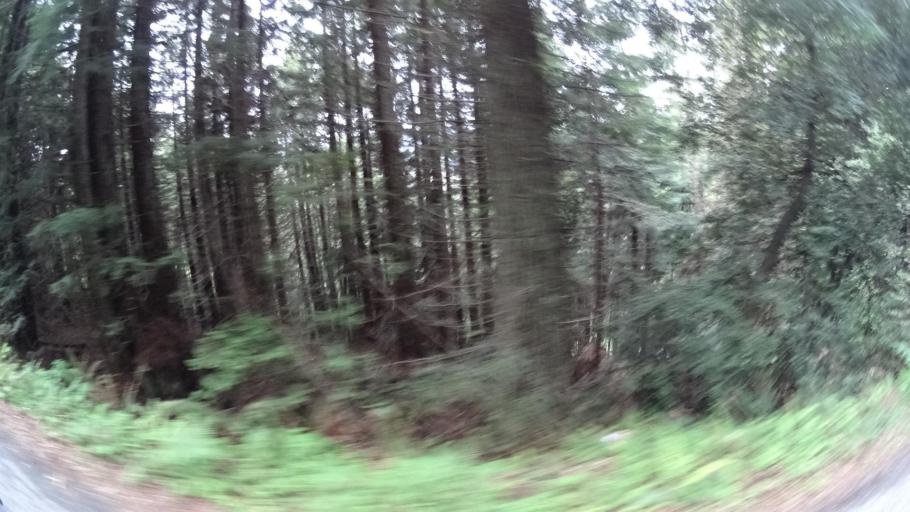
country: US
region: California
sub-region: Humboldt County
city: Blue Lake
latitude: 40.8741
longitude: -123.9769
